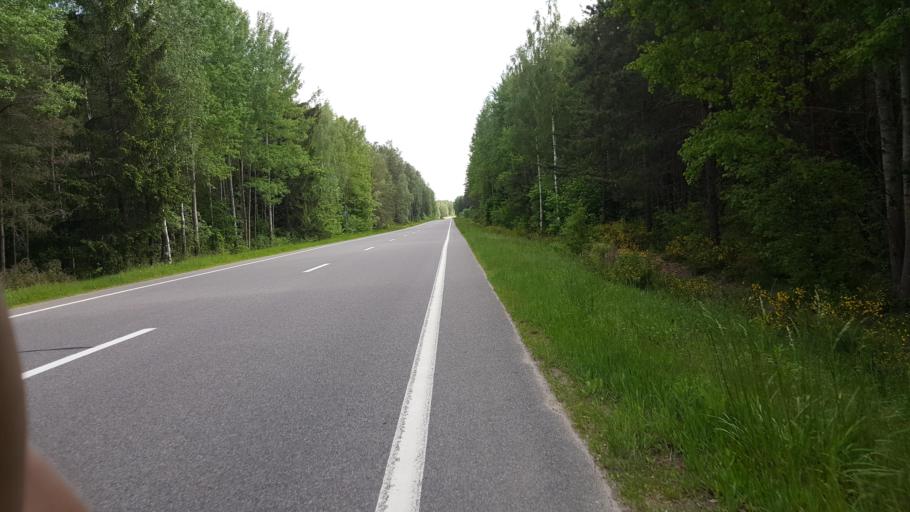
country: BY
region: Brest
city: Pruzhany
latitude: 52.5094
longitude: 24.1780
